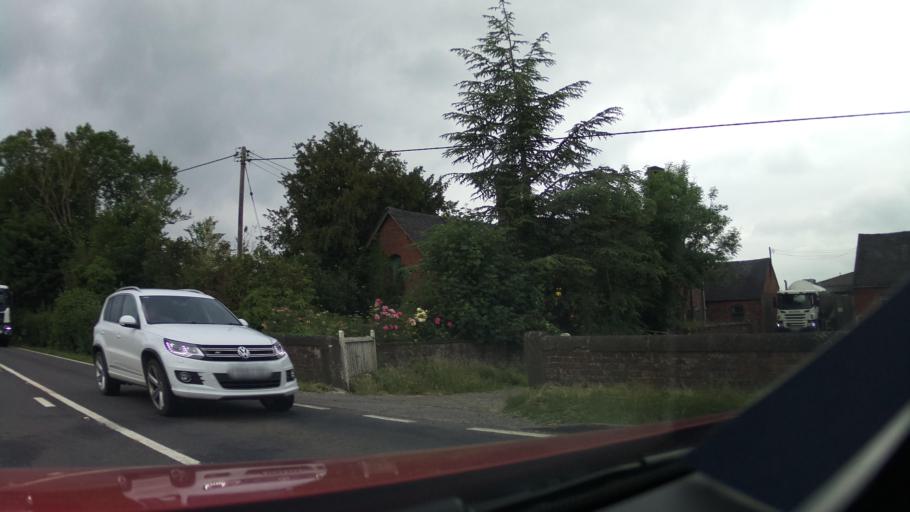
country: GB
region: England
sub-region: Staffordshire
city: Mayfield
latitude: 52.9655
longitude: -1.7569
